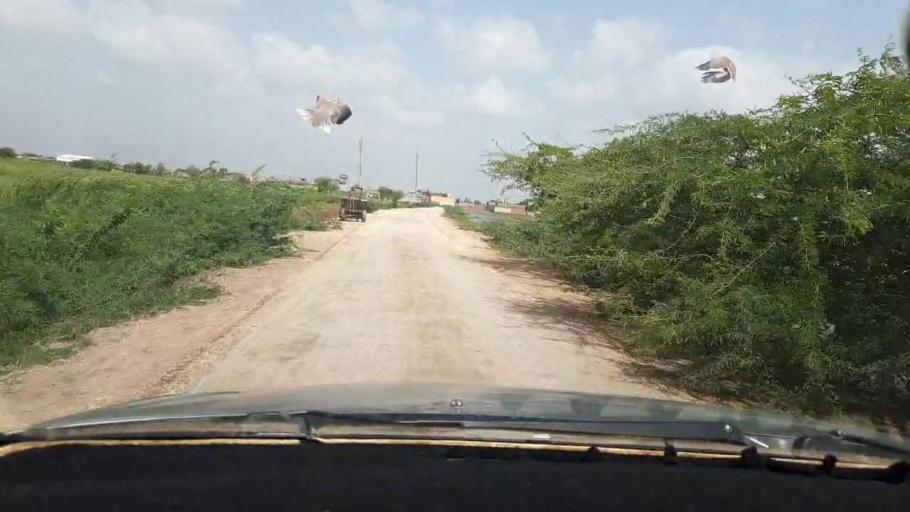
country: PK
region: Sindh
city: Tando Bago
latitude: 24.7573
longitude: 69.1922
